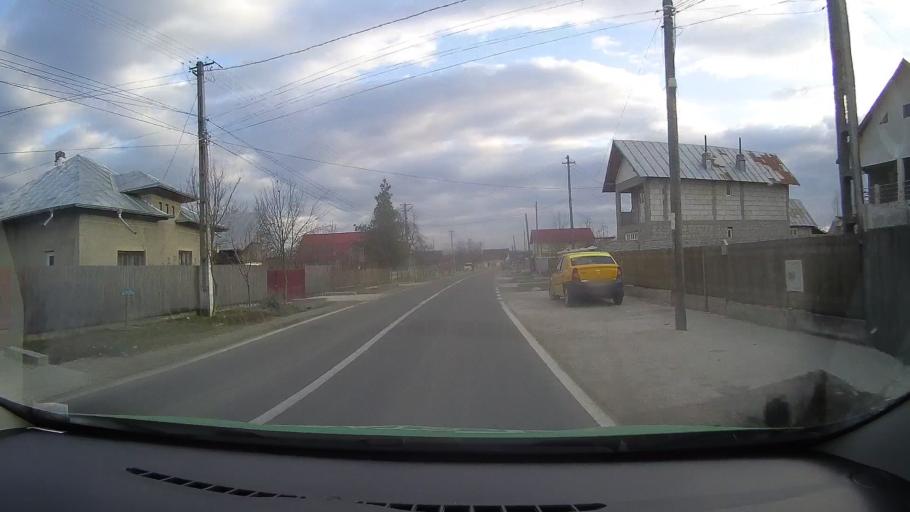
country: RO
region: Dambovita
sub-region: Comuna I. L. Caragiale
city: Mija
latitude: 44.9255
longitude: 25.6906
